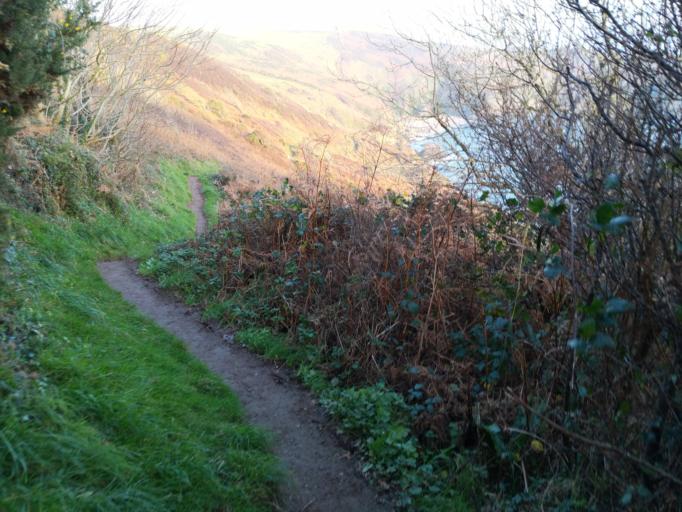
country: GB
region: England
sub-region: Cornwall
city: Fowey
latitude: 50.3284
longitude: -4.6134
